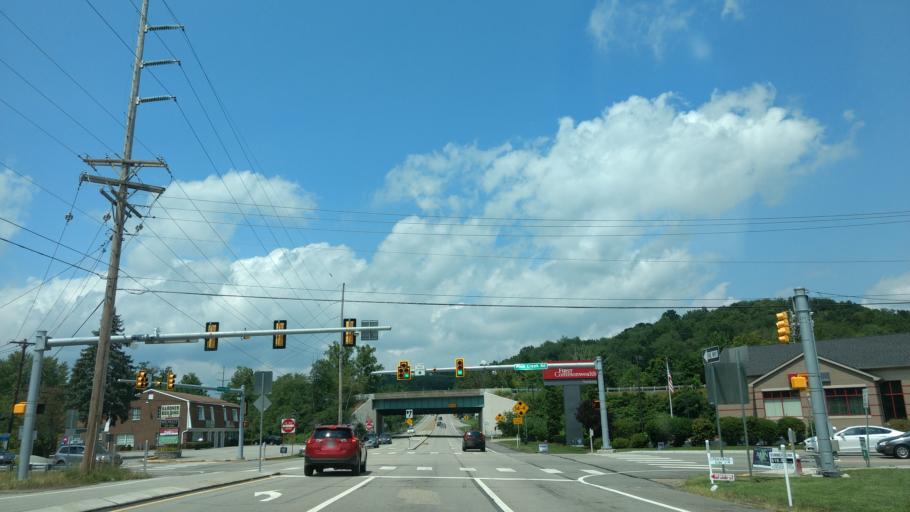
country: US
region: Pennsylvania
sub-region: Allegheny County
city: Franklin Park
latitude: 40.5865
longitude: -80.0449
